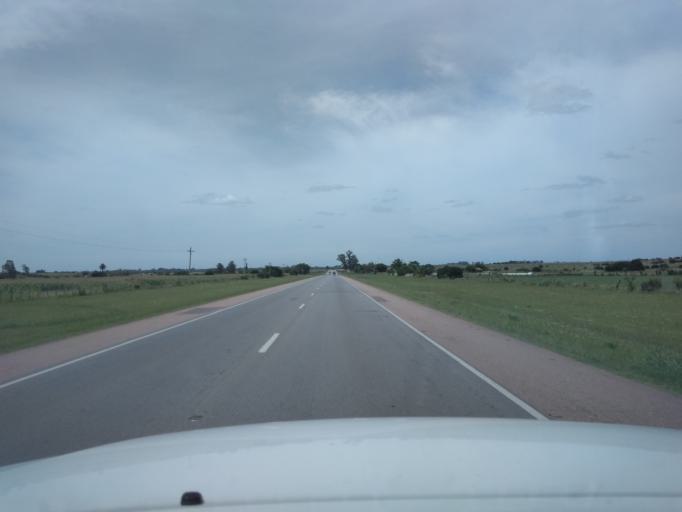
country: UY
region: Canelones
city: Canelones
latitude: -34.3958
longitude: -56.2559
